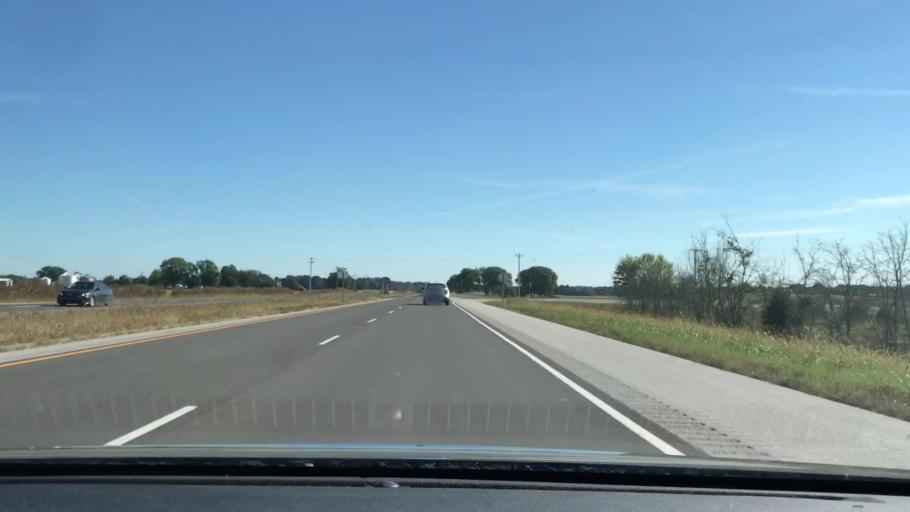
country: US
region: Kentucky
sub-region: Todd County
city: Elkton
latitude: 36.8121
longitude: -87.0324
